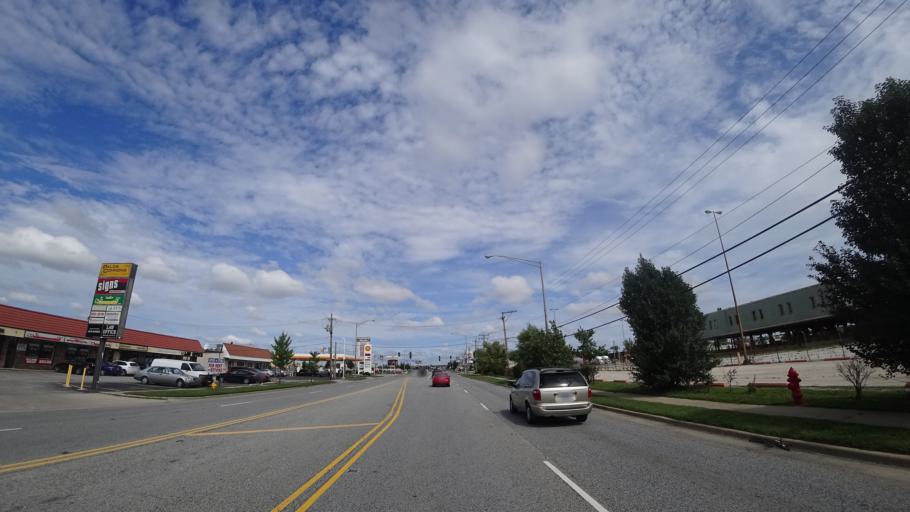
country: US
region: Illinois
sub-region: Cook County
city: Worth
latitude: 41.7030
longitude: -87.7979
